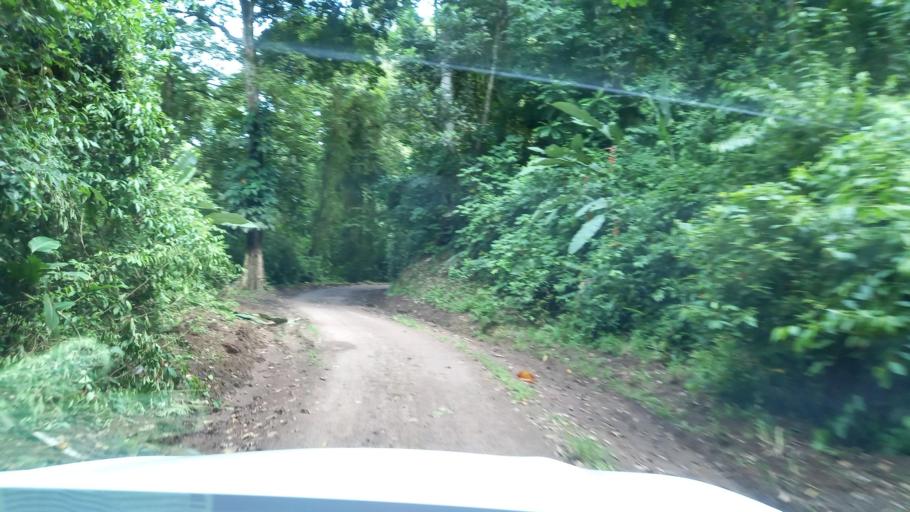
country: NI
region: Jinotega
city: San Jose de Bocay
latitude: 13.3980
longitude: -85.6978
